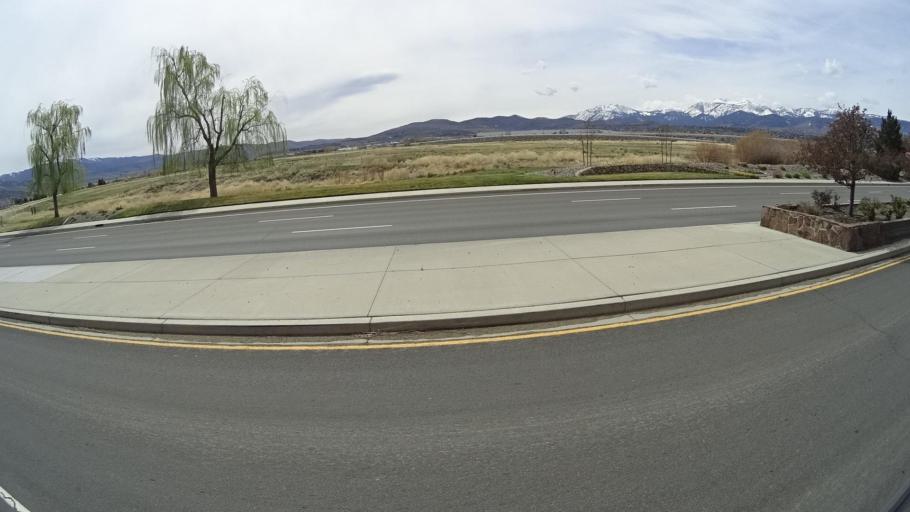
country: US
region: Nevada
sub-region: Washoe County
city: Sparks
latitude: 39.4244
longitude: -119.7447
